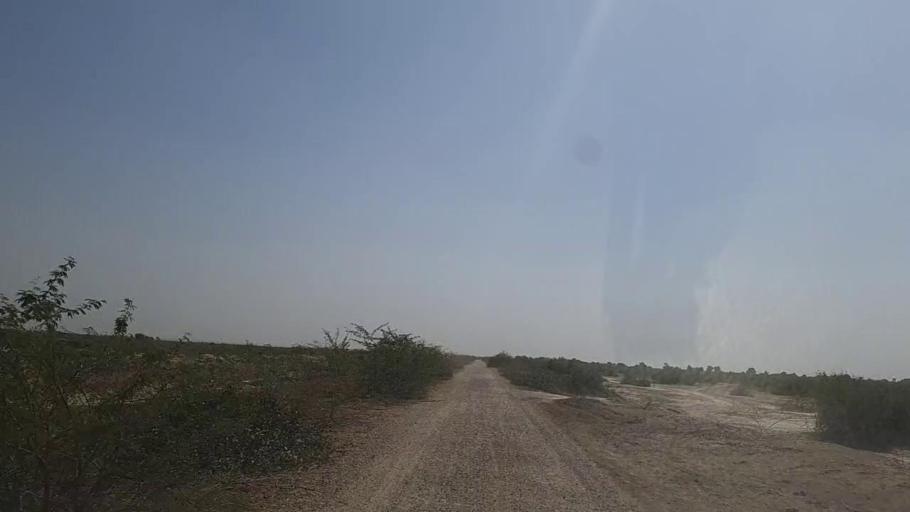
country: PK
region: Sindh
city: Naukot
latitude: 24.6367
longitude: 69.2732
